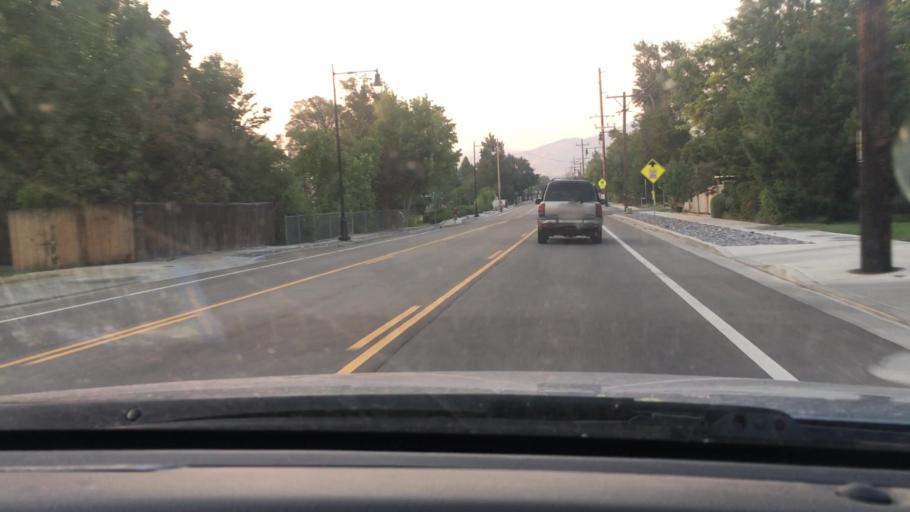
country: US
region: Utah
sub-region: Salt Lake County
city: Canyon Rim
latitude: 40.7037
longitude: -111.8244
